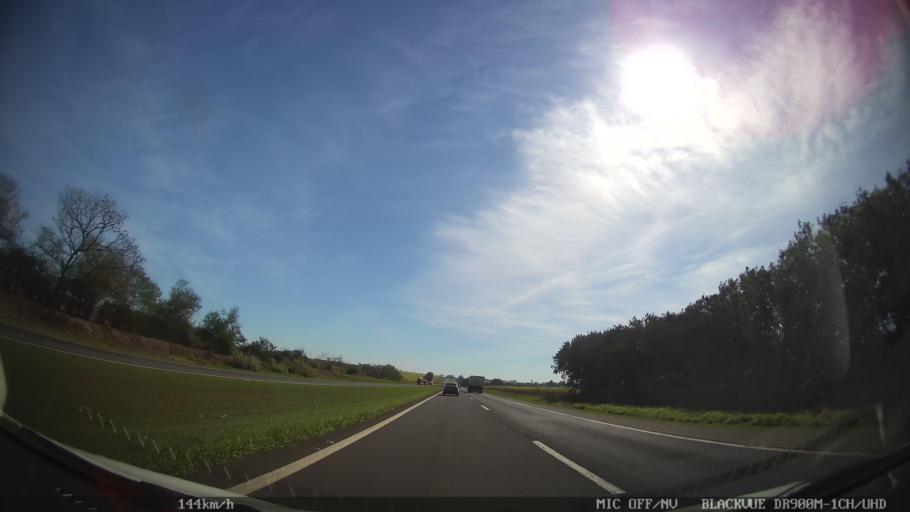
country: BR
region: Sao Paulo
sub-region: Leme
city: Leme
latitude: -22.1226
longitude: -47.4107
